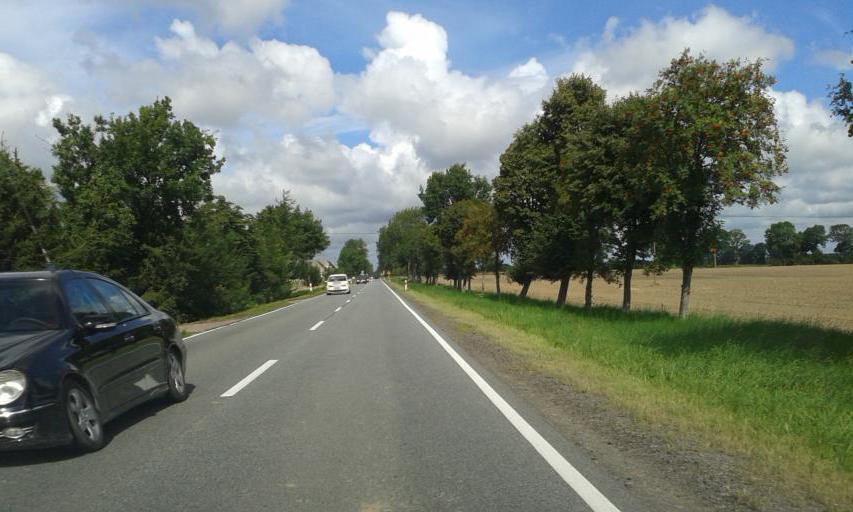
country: PL
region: West Pomeranian Voivodeship
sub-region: Powiat slawienski
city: Slawno
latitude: 54.3302
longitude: 16.5531
